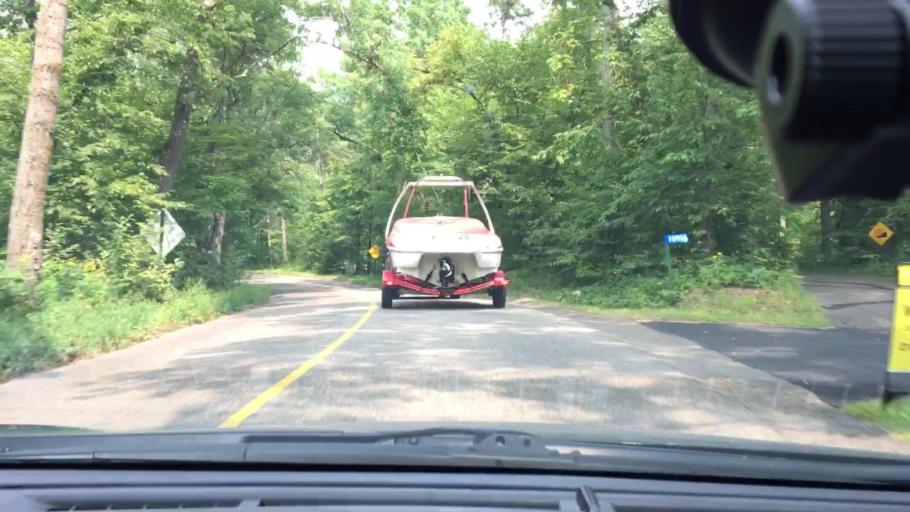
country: US
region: Minnesota
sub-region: Cass County
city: East Gull Lake
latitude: 46.4092
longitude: -94.3544
